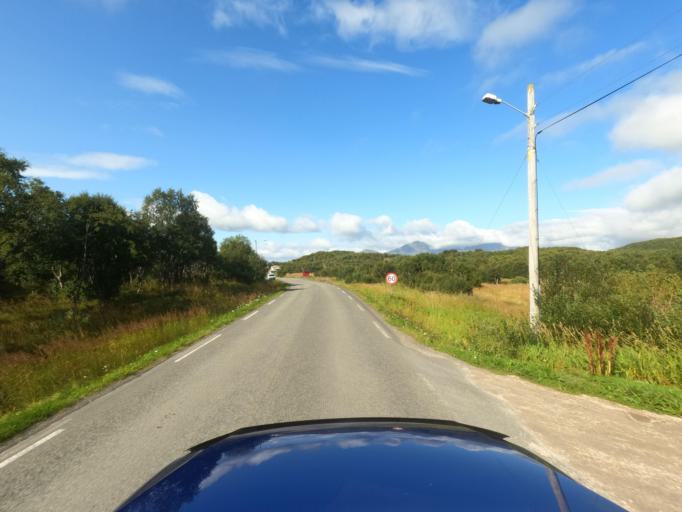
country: NO
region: Nordland
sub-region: Vestvagoy
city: Leknes
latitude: 68.1229
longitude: 13.6463
